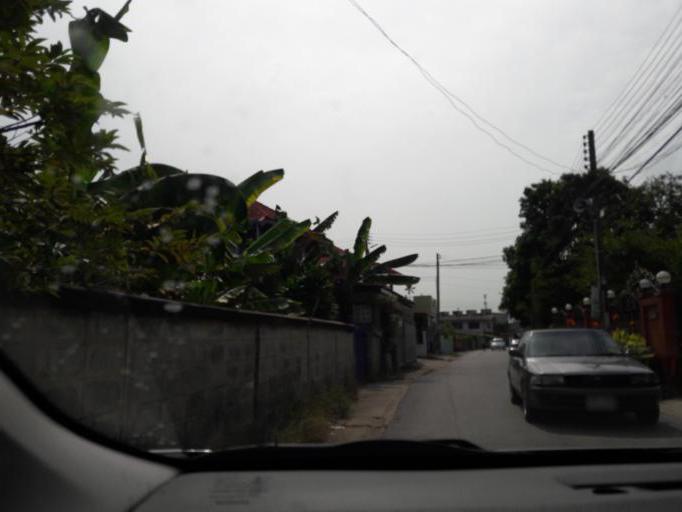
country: TH
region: Ang Thong
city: Ang Thong
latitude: 14.5836
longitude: 100.4629
